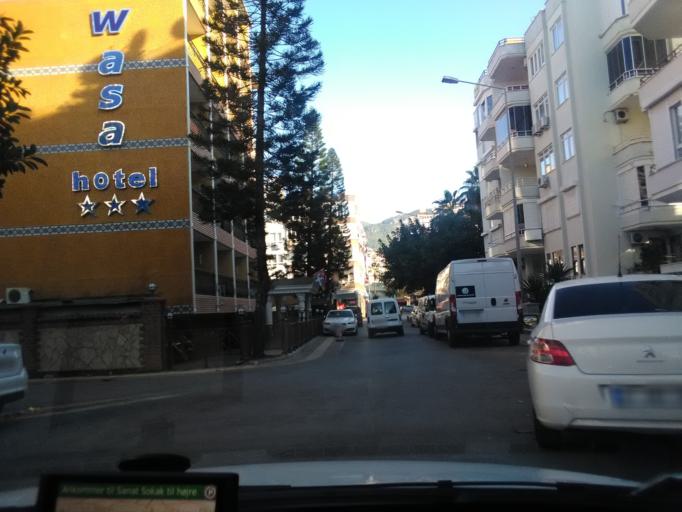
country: TR
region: Antalya
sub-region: Alanya
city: Alanya
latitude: 36.5446
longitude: 31.9903
